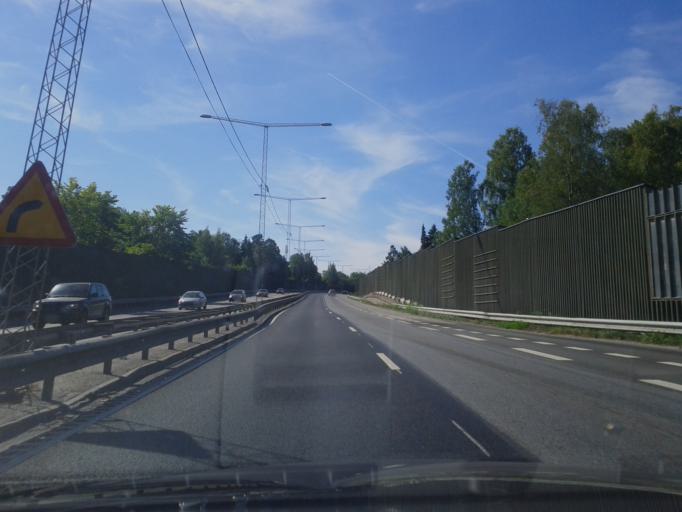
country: SE
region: Stockholm
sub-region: Taby Kommun
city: Taby
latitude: 59.4305
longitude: 18.0654
